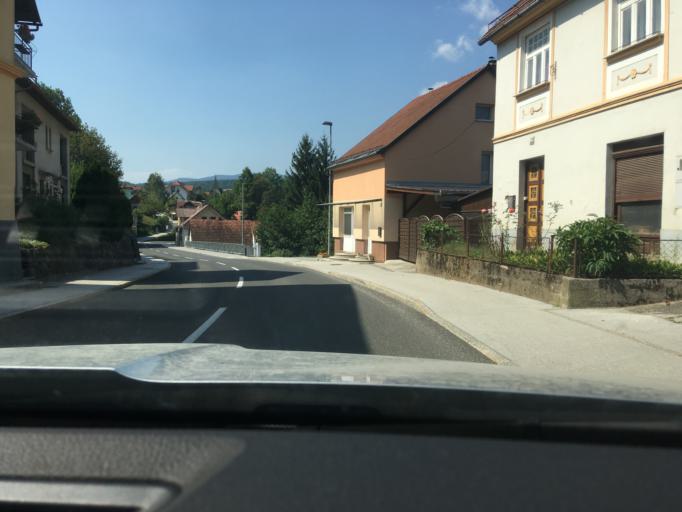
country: SI
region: Metlika
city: Metlika
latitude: 45.6485
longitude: 15.3176
